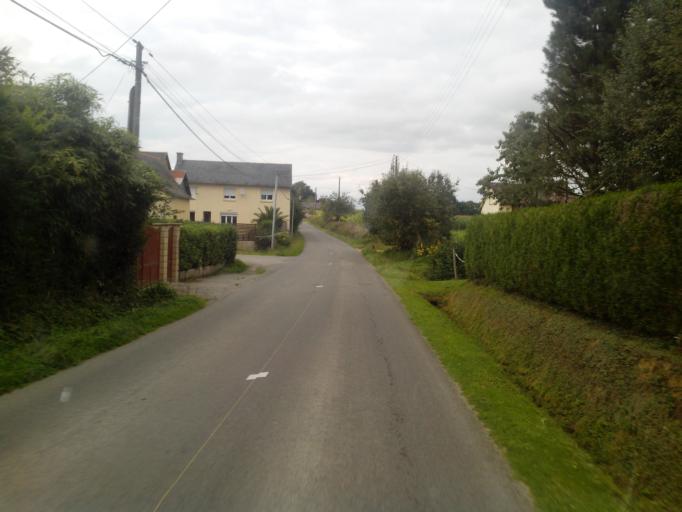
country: FR
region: Brittany
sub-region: Departement d'Ille-et-Vilaine
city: Melesse
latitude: 48.2289
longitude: -1.6875
